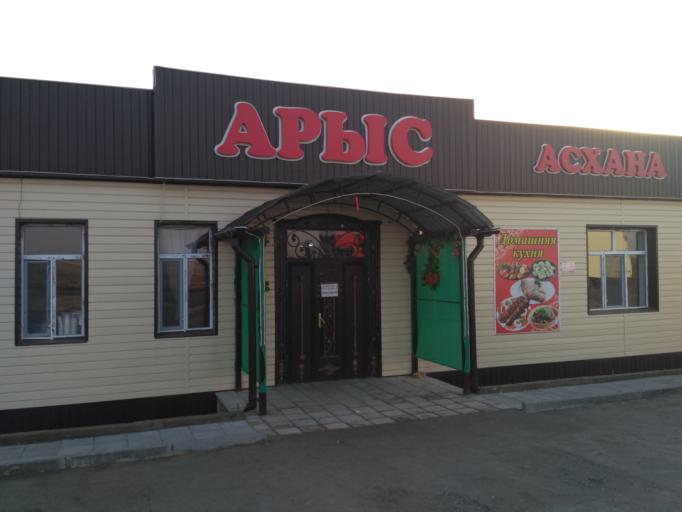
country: KZ
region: Ongtustik Qazaqstan
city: Temirlanovka
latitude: 42.5698
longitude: 69.3111
